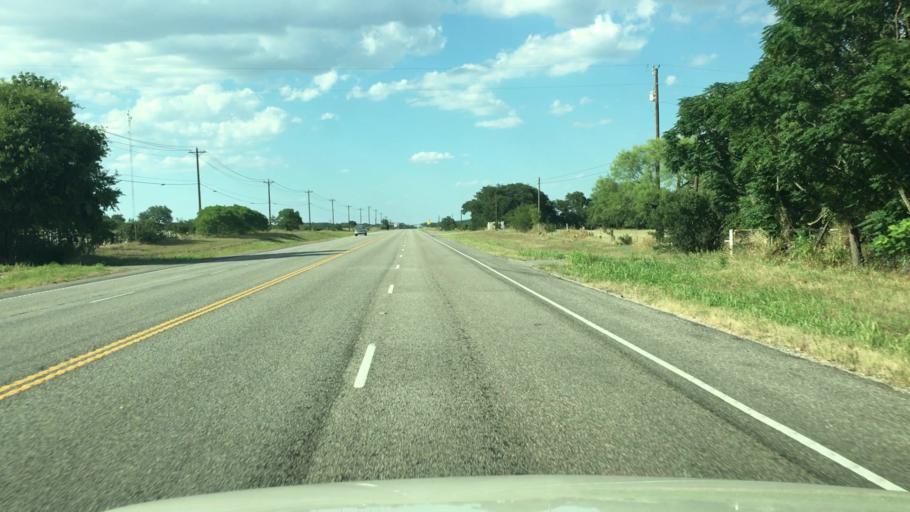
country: US
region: Texas
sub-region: Llano County
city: Horseshoe Bay
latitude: 30.4174
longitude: -98.3502
